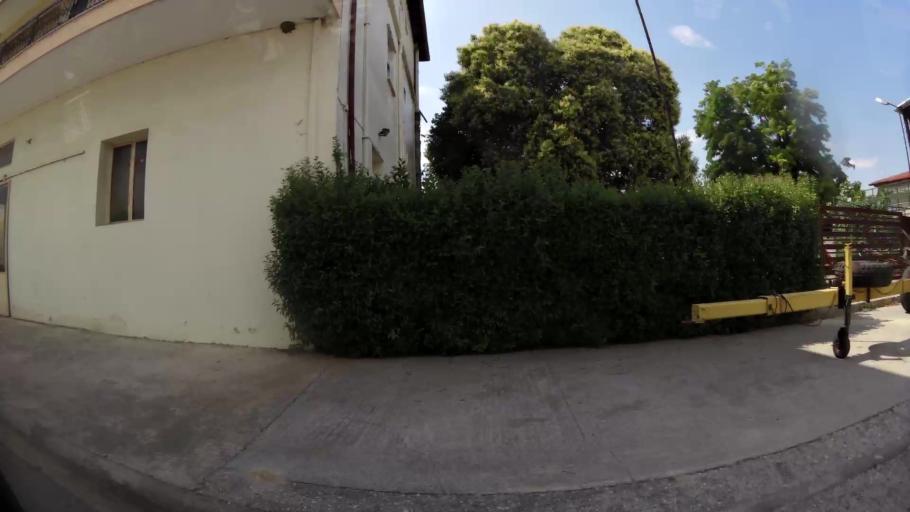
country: GR
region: Central Macedonia
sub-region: Nomos Pierias
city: Korinos
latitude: 40.3181
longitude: 22.5857
